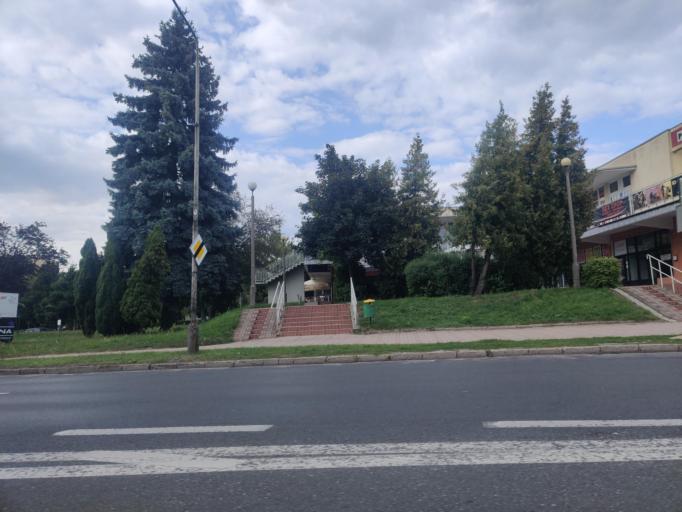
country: PL
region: Greater Poland Voivodeship
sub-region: Konin
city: Konin
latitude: 52.2275
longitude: 18.2637
